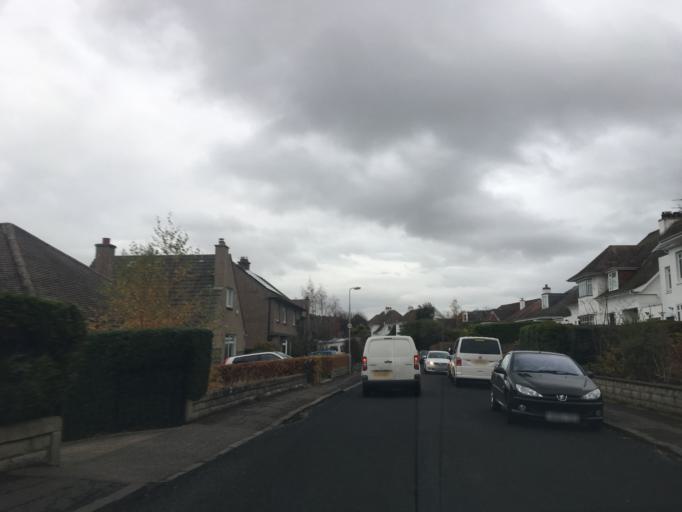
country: GB
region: Scotland
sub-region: Edinburgh
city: Colinton
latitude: 55.9077
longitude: -3.2149
